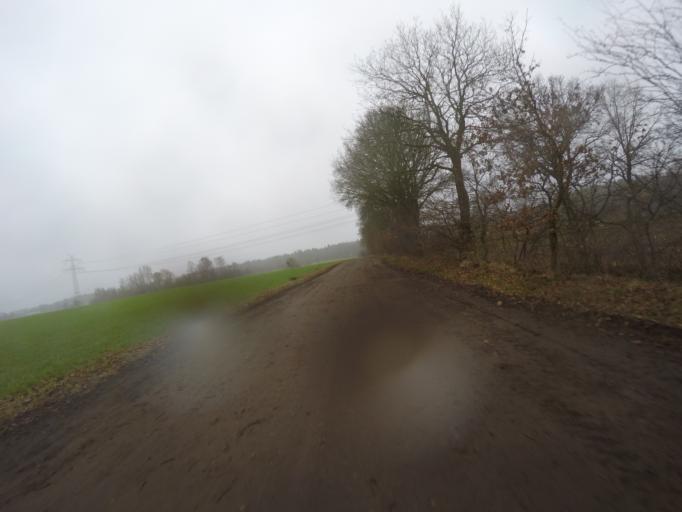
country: DE
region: Schleswig-Holstein
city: Ellerau
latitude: 53.7426
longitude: 9.9244
